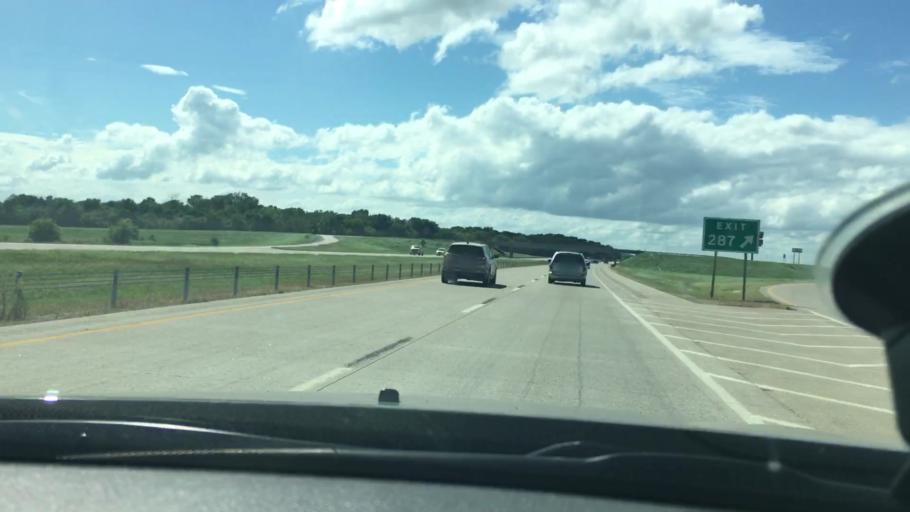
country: US
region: Oklahoma
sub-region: Muskogee County
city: Warner
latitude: 35.4825
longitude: -95.1452
